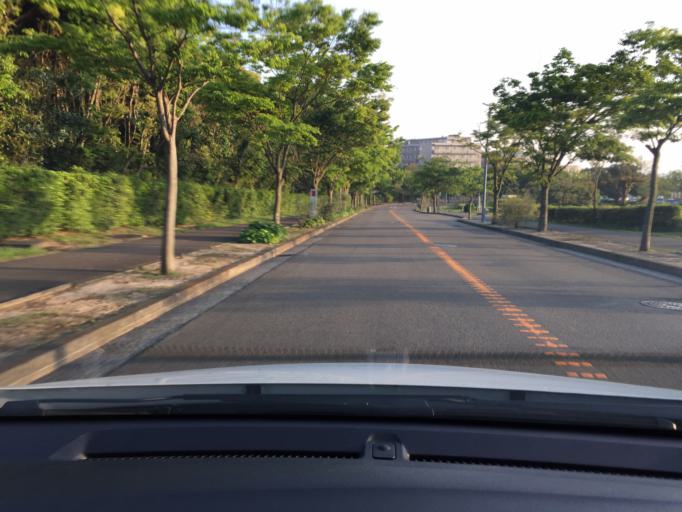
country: JP
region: Kanagawa
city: Hayama
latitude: 35.2588
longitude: 139.6065
